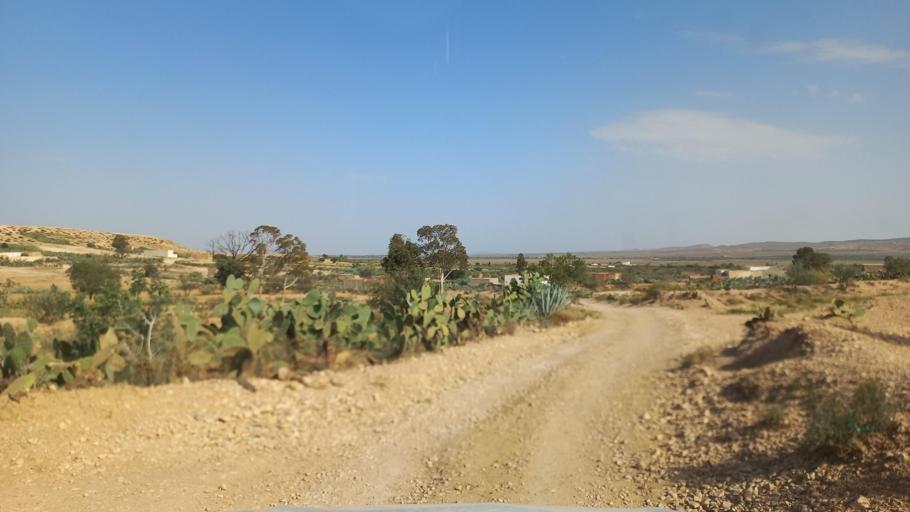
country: TN
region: Al Qasrayn
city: Kasserine
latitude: 35.2565
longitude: 8.9264
